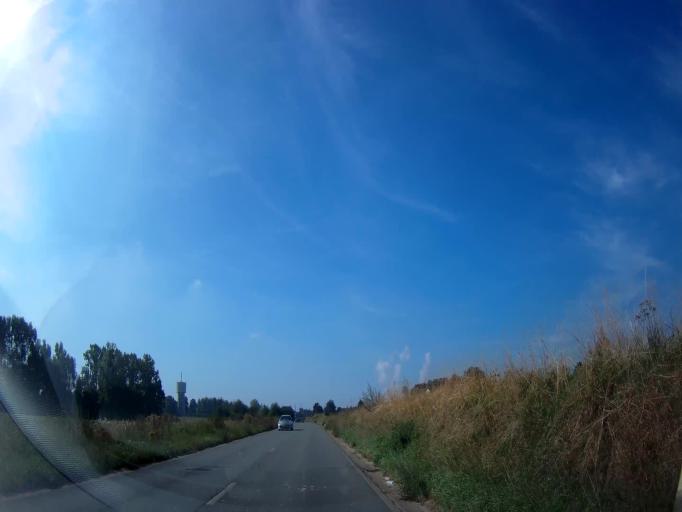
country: BE
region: Wallonia
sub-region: Province de Liege
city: Verlaine
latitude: 50.5969
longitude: 5.3435
